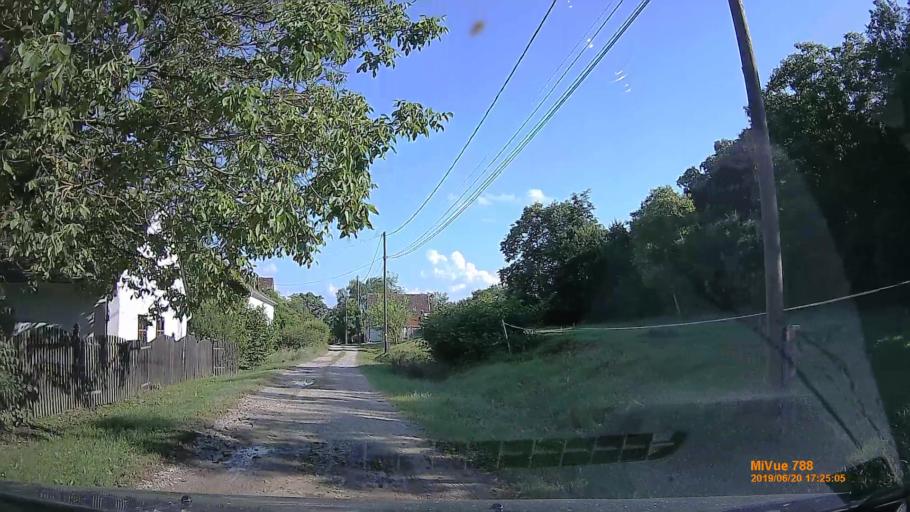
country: HU
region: Baranya
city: Buekkoesd
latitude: 46.1636
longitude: 18.0091
